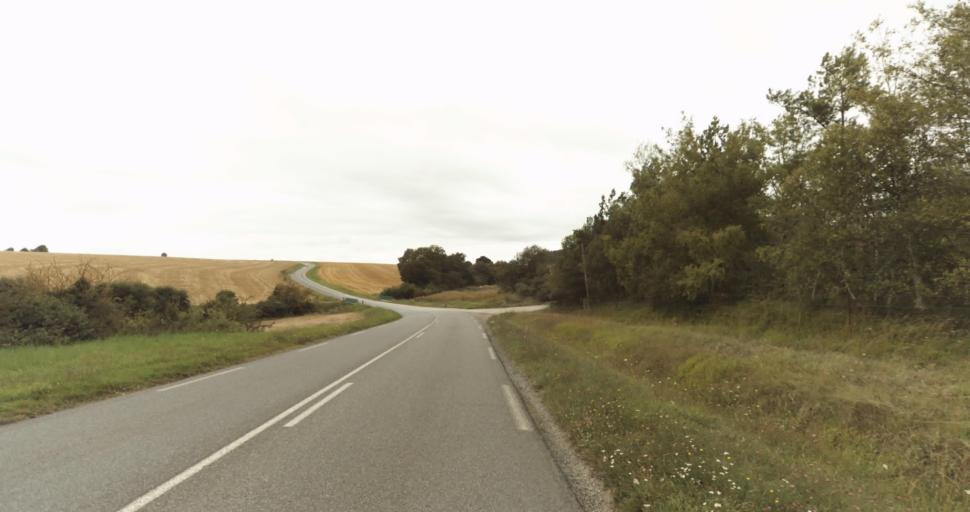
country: FR
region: Haute-Normandie
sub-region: Departement de l'Eure
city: Gravigny
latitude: 49.0568
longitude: 1.2575
